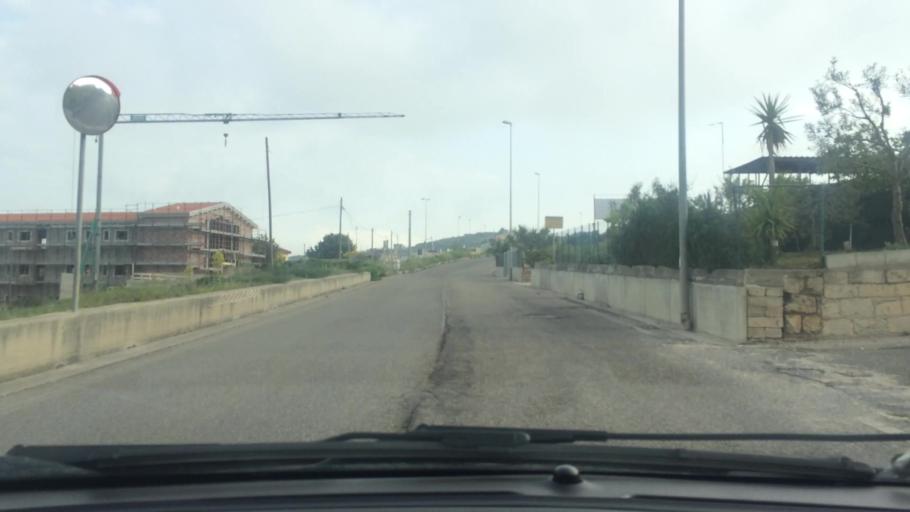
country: IT
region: Basilicate
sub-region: Provincia di Matera
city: Matera
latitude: 40.6839
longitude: 16.5734
